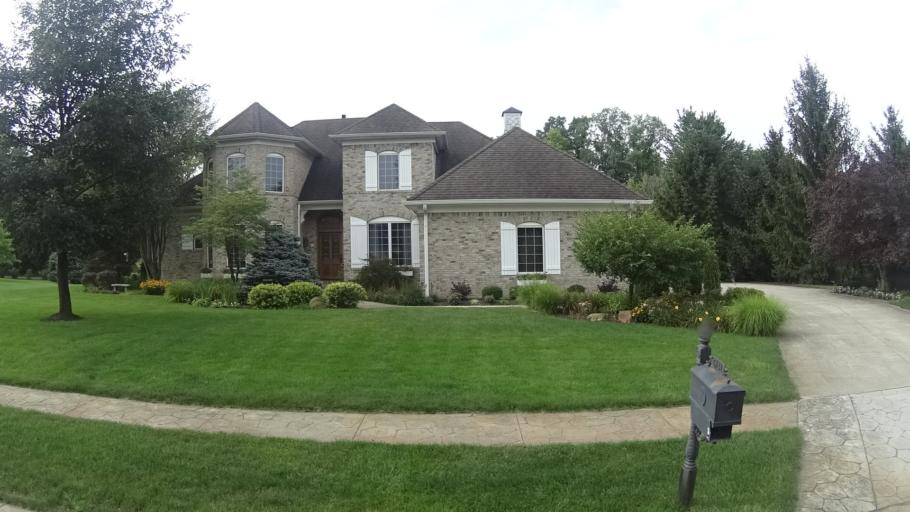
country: US
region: Indiana
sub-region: Madison County
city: Pendleton
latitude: 40.0049
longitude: -85.7895
